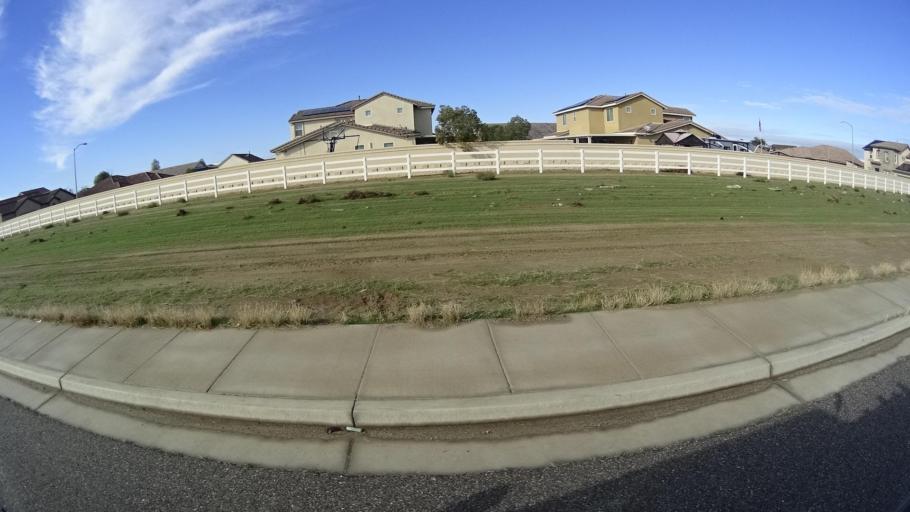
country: US
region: California
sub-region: Kern County
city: Rosedale
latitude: 35.3934
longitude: -119.1724
